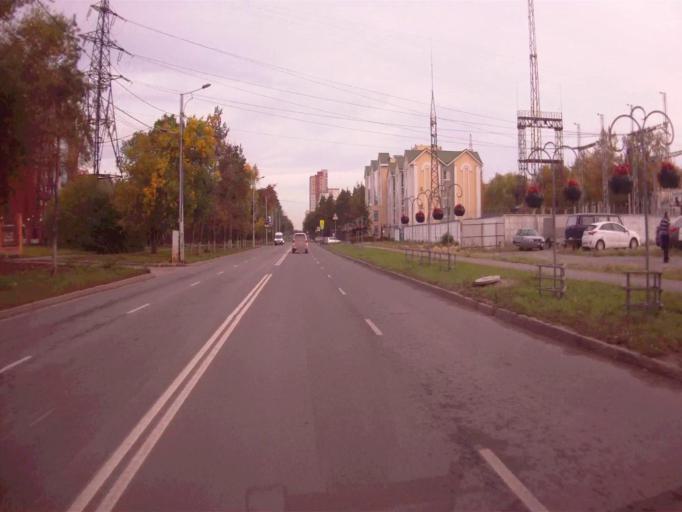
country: RU
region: Chelyabinsk
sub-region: Gorod Chelyabinsk
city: Chelyabinsk
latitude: 55.1494
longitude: 61.3653
